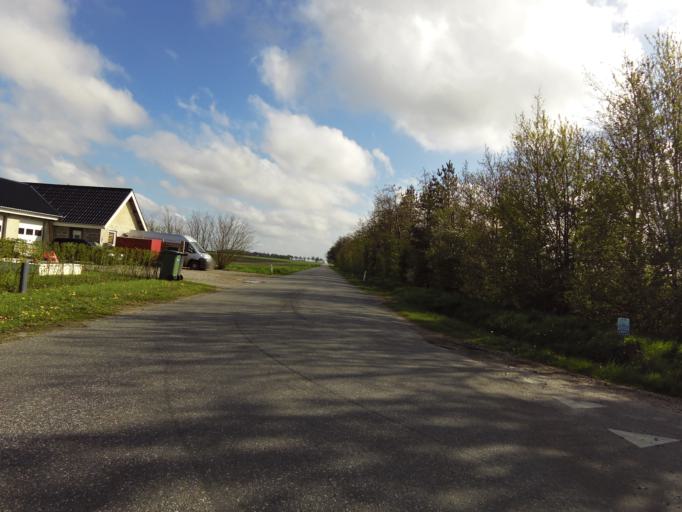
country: DK
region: South Denmark
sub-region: Haderslev Kommune
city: Gram
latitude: 55.3350
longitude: 8.9838
